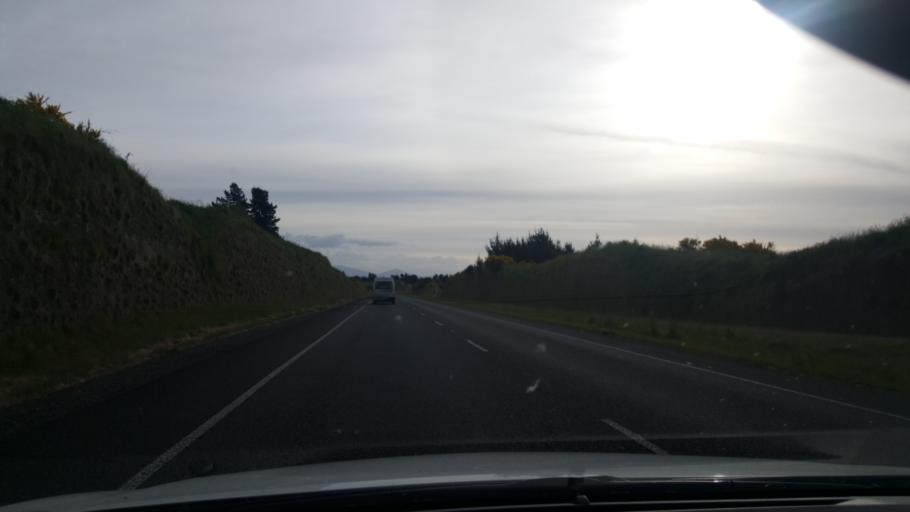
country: NZ
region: Waikato
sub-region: Taupo District
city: Taupo
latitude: -38.7302
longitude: 176.0854
